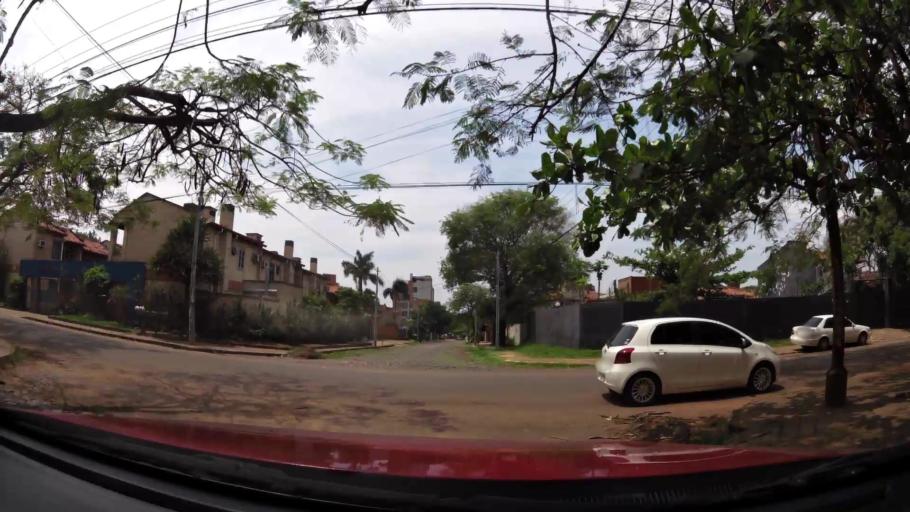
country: PY
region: Central
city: Fernando de la Mora
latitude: -25.3093
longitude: -57.5588
